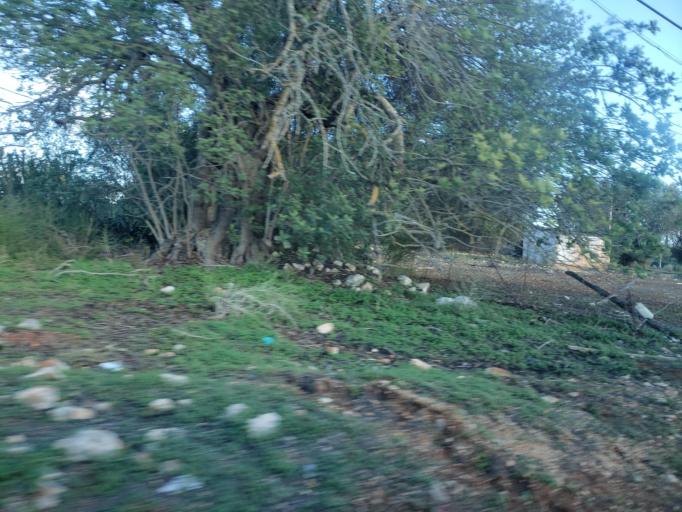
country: PT
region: Faro
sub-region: Portimao
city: Alvor
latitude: 37.1903
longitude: -8.5882
